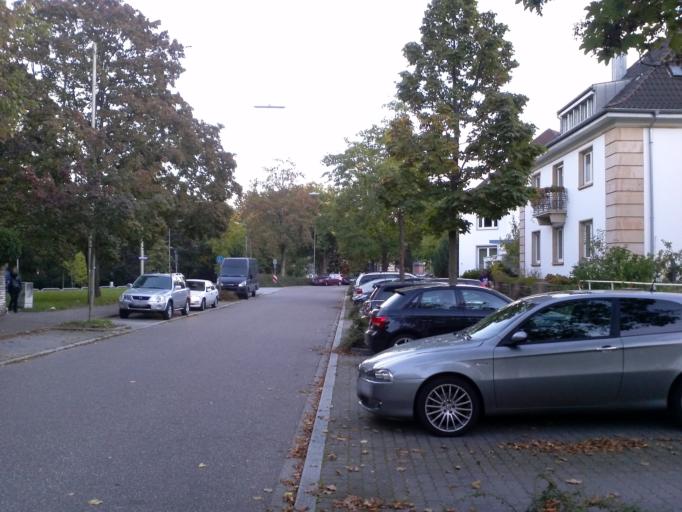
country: DE
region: Baden-Wuerttemberg
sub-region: Karlsruhe Region
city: Karlsruhe
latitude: 48.9960
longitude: 8.3954
